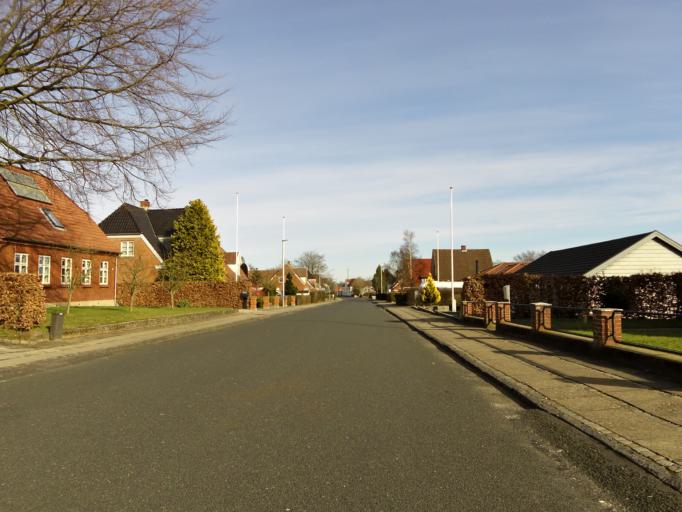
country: DK
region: South Denmark
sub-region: Kolding Kommune
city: Vamdrup
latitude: 55.3566
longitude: 9.1935
